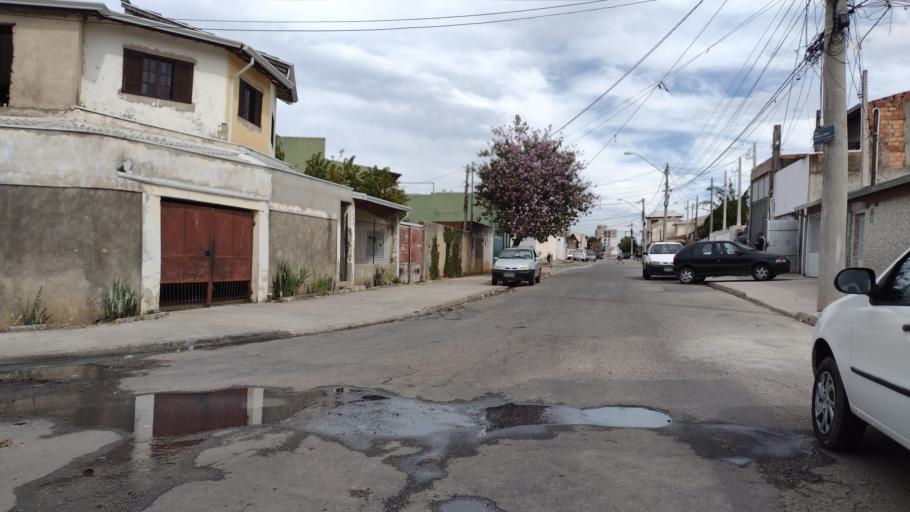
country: BR
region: Sao Paulo
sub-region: Sorocaba
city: Sorocaba
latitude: -23.4302
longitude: -47.4678
